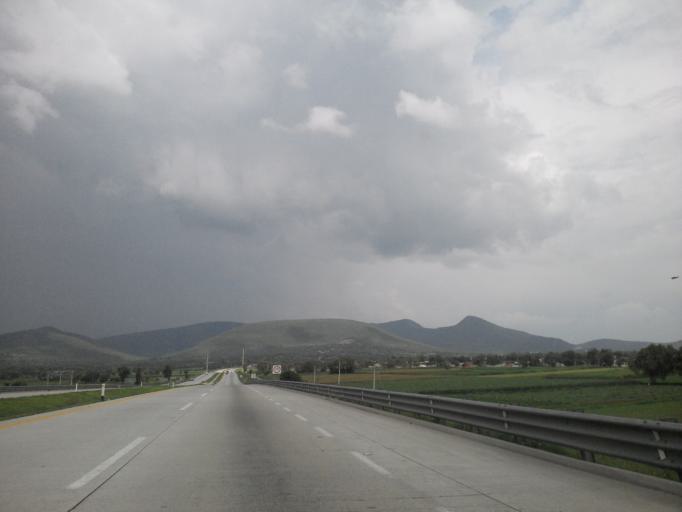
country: MX
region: Hidalgo
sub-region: Atitalaquia
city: Tezoquipa
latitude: 20.0636
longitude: -99.2091
